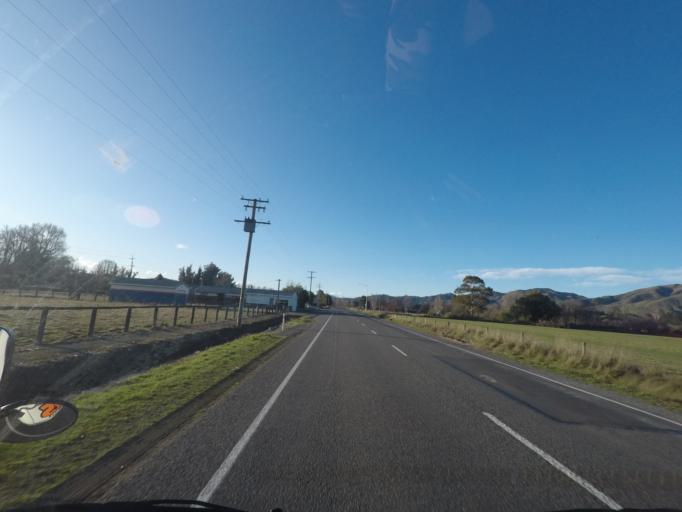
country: NZ
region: Canterbury
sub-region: Kaikoura District
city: Kaikoura
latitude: -42.7141
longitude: 173.2900
